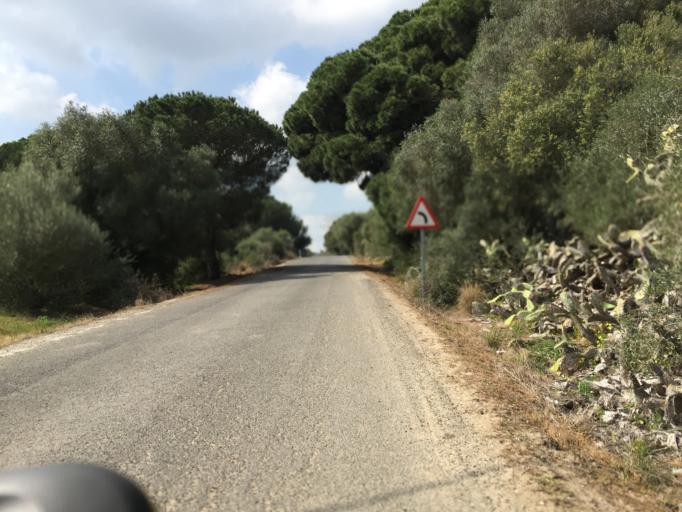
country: ES
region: Andalusia
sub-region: Provincia de Cadiz
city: Vejer de la Frontera
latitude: 36.2816
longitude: -5.9319
